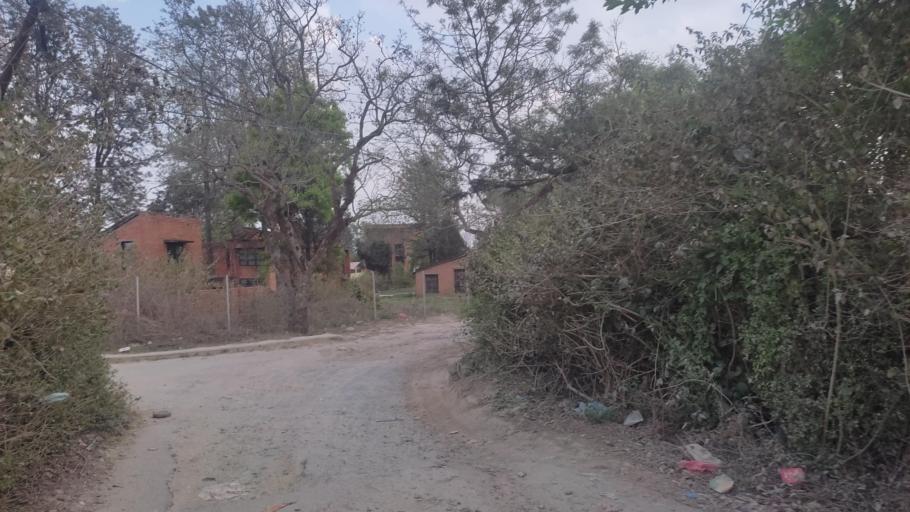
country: NP
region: Central Region
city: Kirtipur
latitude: 27.6841
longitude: 85.2836
